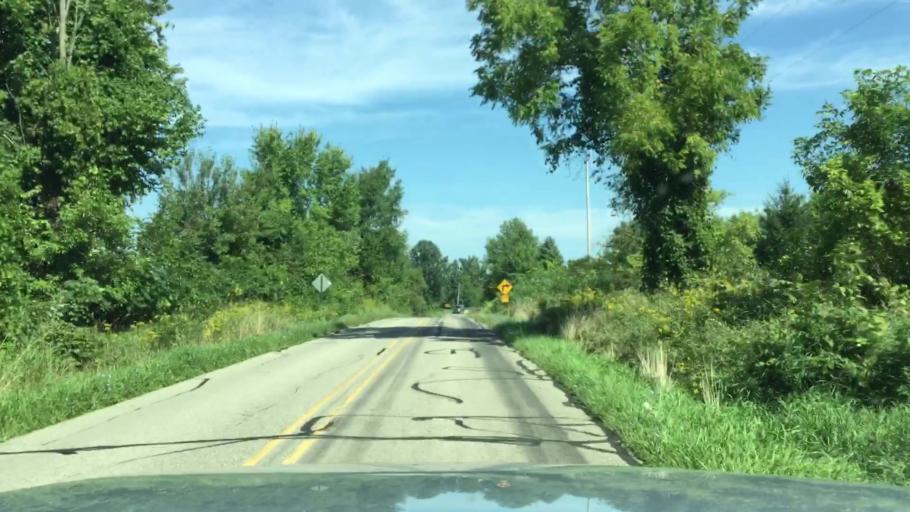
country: US
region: Michigan
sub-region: Lenawee County
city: Manitou Beach-Devils Lake
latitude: 41.9945
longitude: -84.3251
